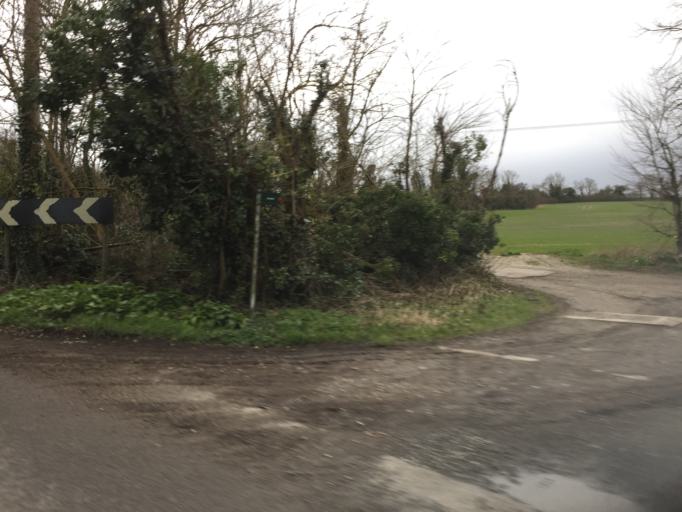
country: GB
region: England
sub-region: Oxfordshire
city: Blewbury
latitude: 51.5765
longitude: -1.2627
